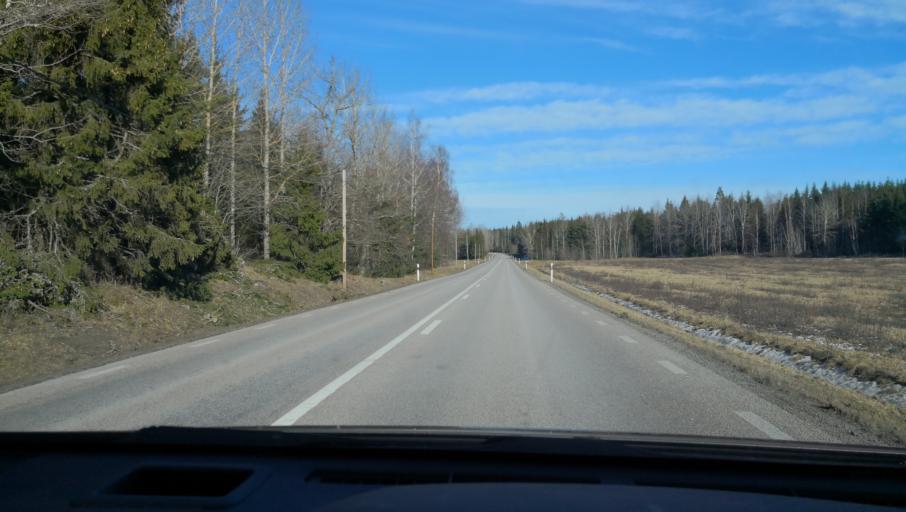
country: SE
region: Uppsala
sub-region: Osthammars Kommun
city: Osterbybruk
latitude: 60.1232
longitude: 17.8066
